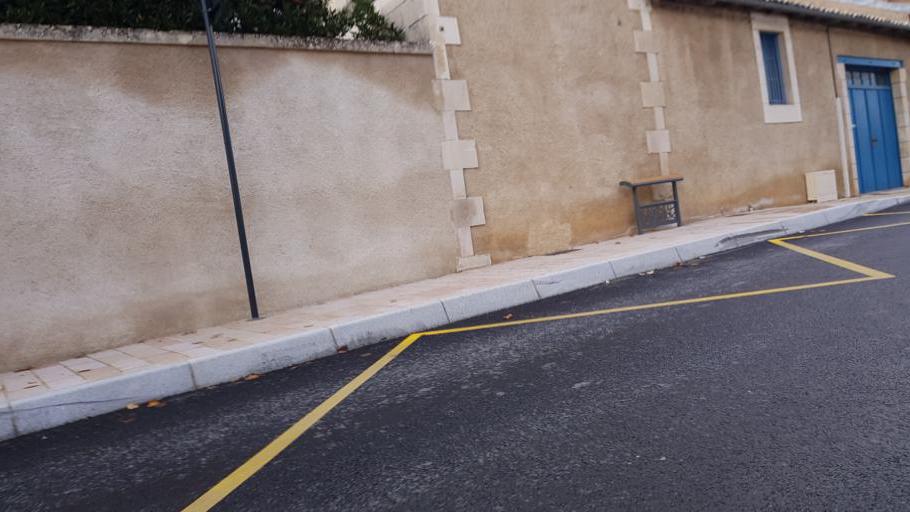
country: FR
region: Poitou-Charentes
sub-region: Departement de la Vienne
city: Chasseneuil-du-Poitou
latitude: 46.6482
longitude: 0.3727
